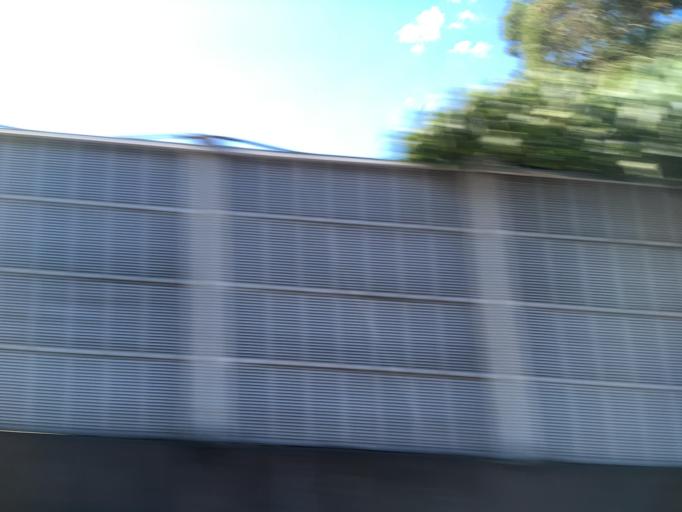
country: TW
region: Taipei
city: Taipei
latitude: 25.0223
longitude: 121.5769
